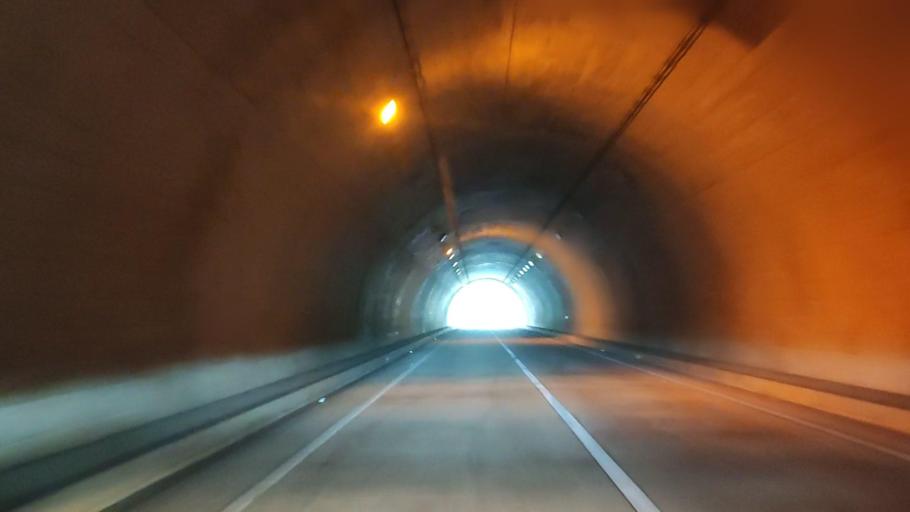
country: JP
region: Shizuoka
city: Heda
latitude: 34.9108
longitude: 138.8480
